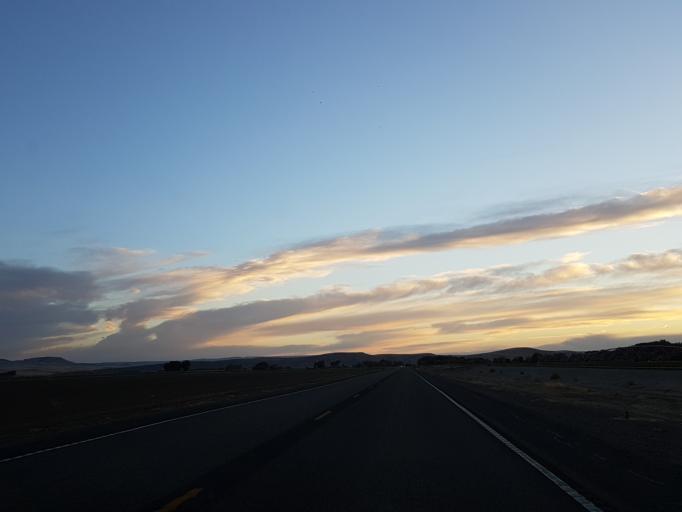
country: US
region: Oregon
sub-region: Malheur County
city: Vale
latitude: 43.9499
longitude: -117.2948
